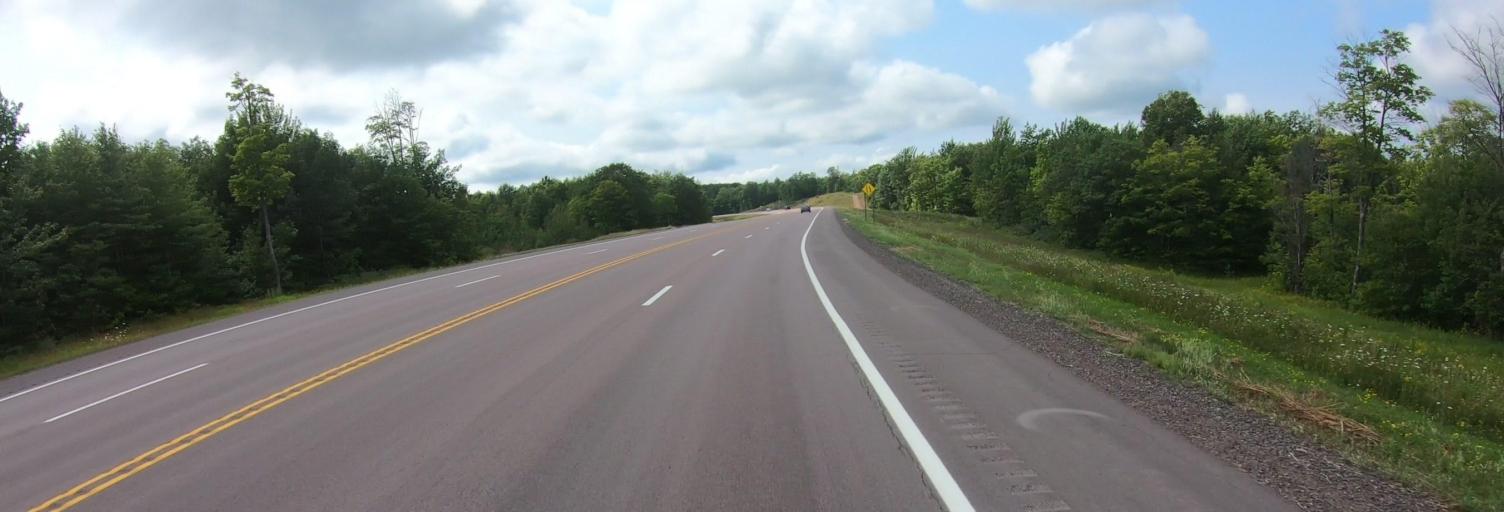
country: US
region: Michigan
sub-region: Houghton County
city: Hancock
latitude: 47.0594
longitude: -88.6491
